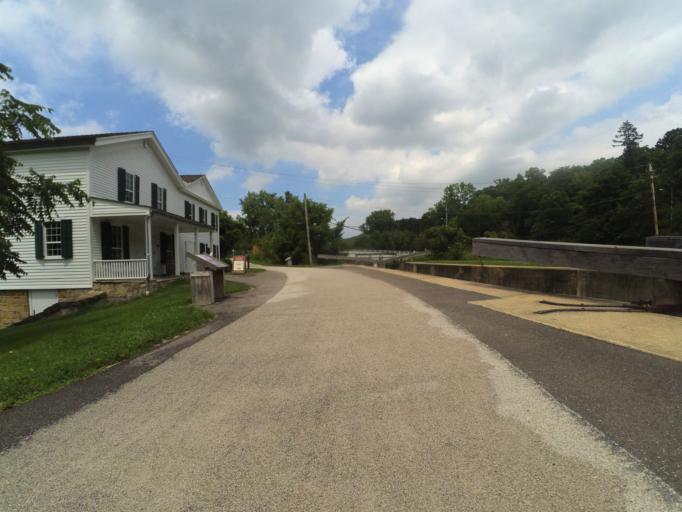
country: US
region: Ohio
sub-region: Cuyahoga County
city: Valley View
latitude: 41.3724
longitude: -81.6129
